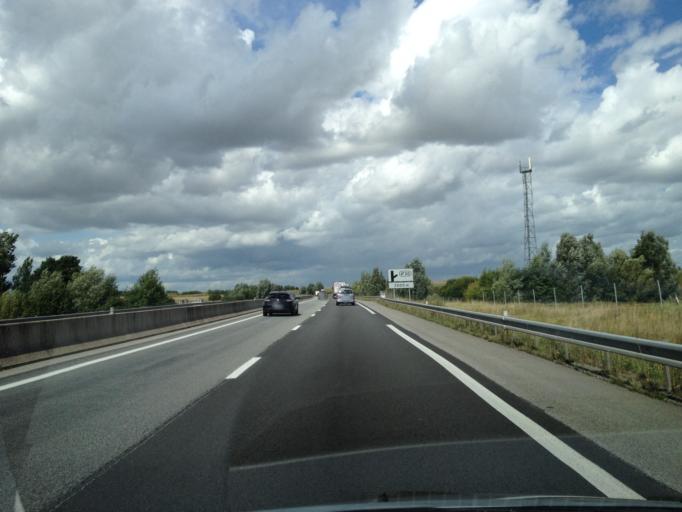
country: FR
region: Pays de la Loire
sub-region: Departement de la Sarthe
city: Beaumont-sur-Sarthe
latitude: 48.2950
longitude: 0.1534
